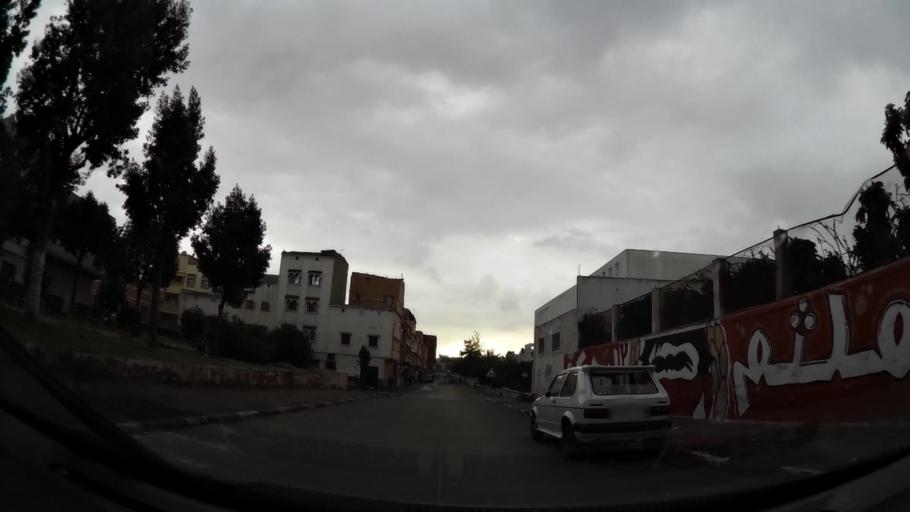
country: MA
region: Grand Casablanca
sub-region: Casablanca
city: Casablanca
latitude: 33.5504
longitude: -7.6000
